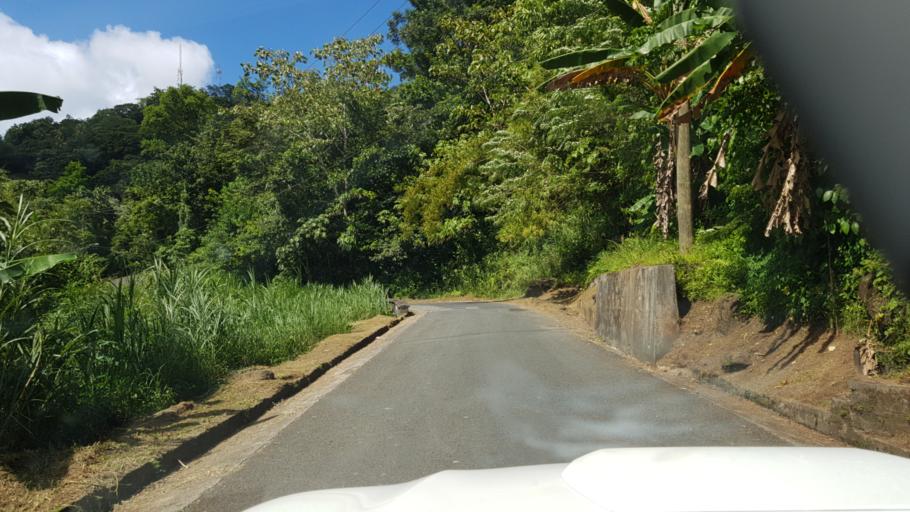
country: LC
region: Castries Quarter
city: Castries
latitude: 13.9912
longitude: -60.9737
